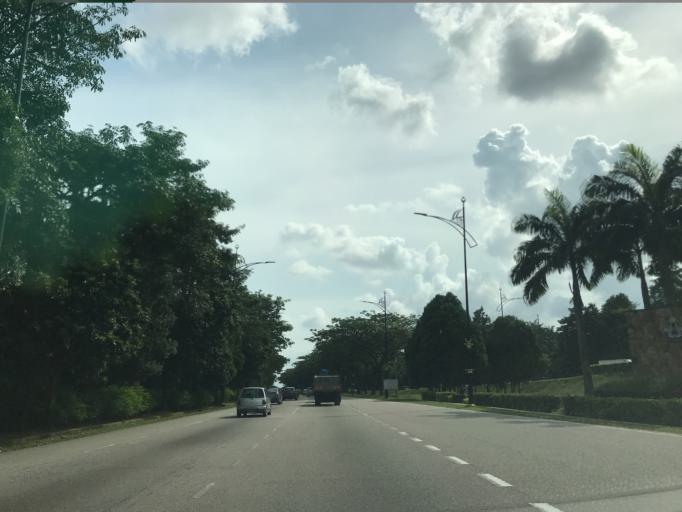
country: MY
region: Johor
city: Skudai
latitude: 1.5577
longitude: 103.6592
